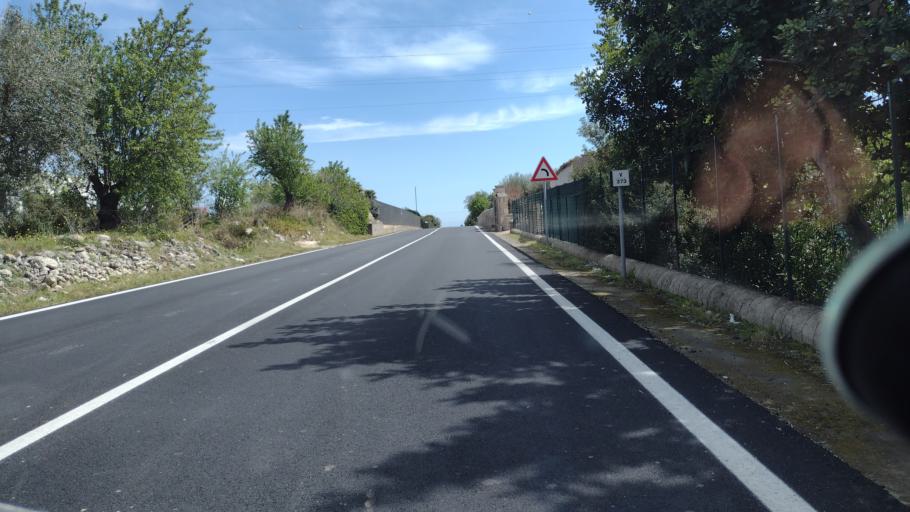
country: IT
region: Sicily
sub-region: Provincia di Siracusa
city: Noto
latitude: 36.8779
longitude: 15.0455
